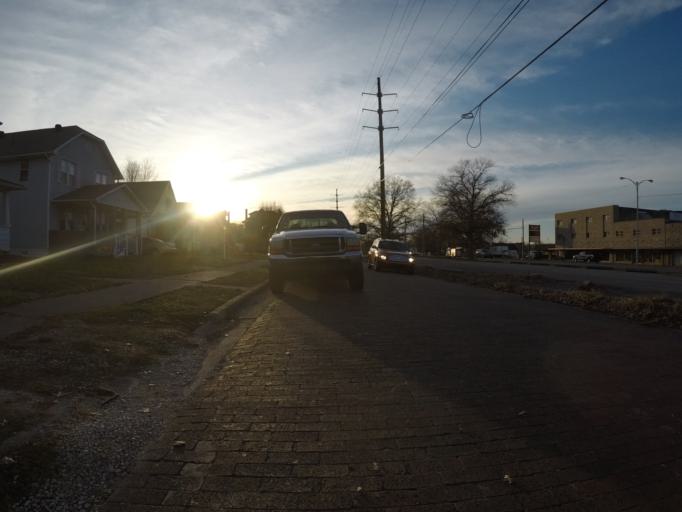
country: US
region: Ohio
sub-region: Lawrence County
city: Burlington
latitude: 38.4012
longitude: -82.5092
